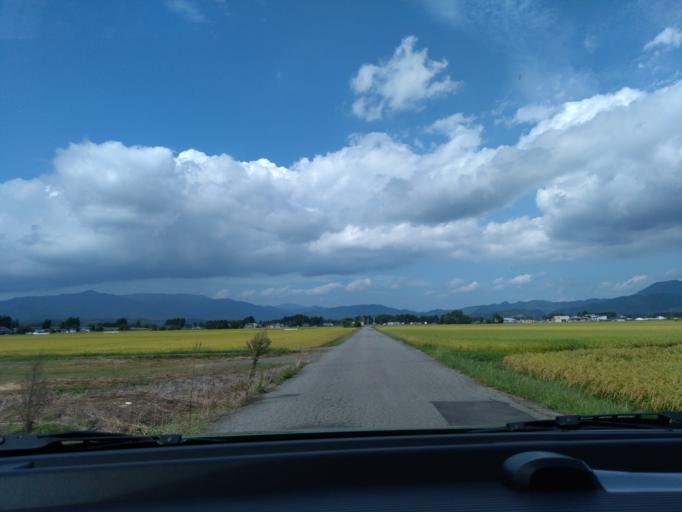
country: JP
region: Akita
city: Kakunodatemachi
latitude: 39.6061
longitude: 140.5849
